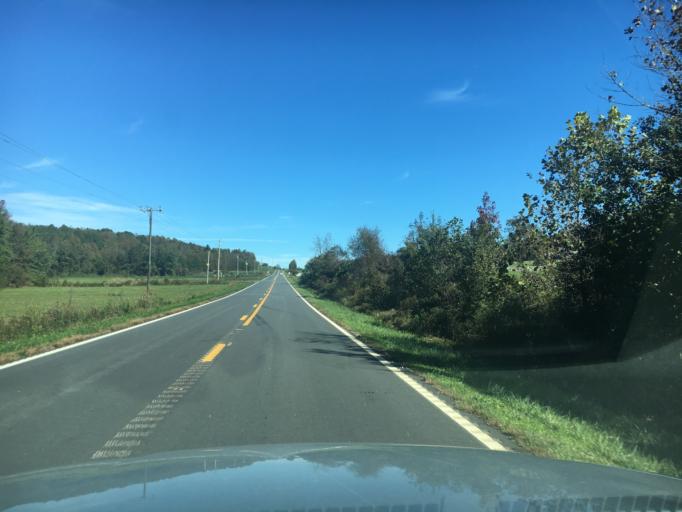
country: US
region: North Carolina
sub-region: Burke County
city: Glen Alpine
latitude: 35.6295
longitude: -81.7998
